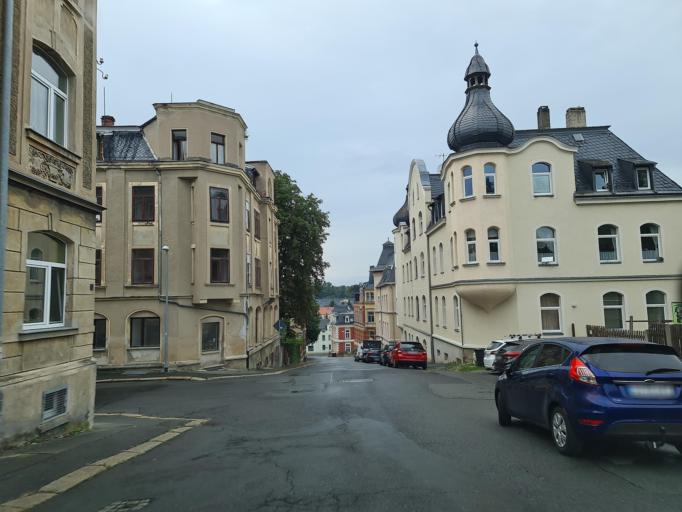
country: DE
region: Saxony
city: Oelsnitz
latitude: 50.4172
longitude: 12.1785
